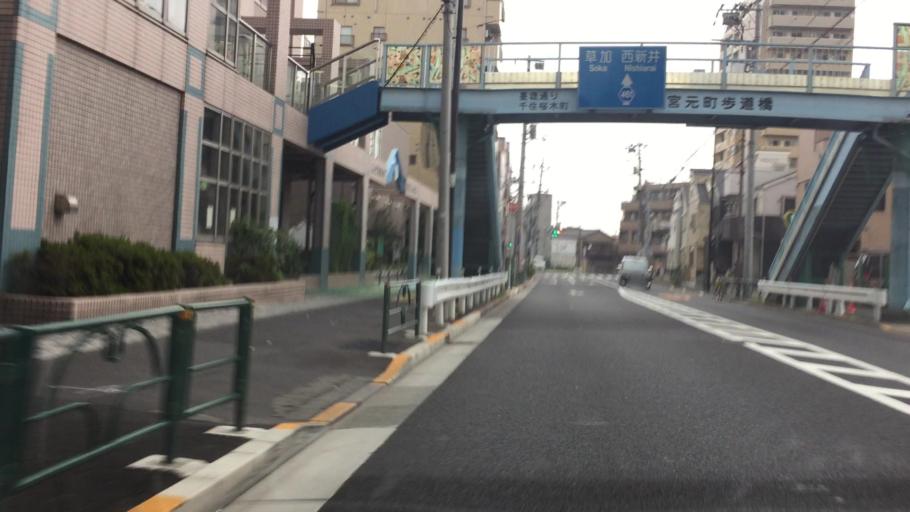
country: JP
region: Saitama
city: Soka
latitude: 35.7498
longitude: 139.7944
